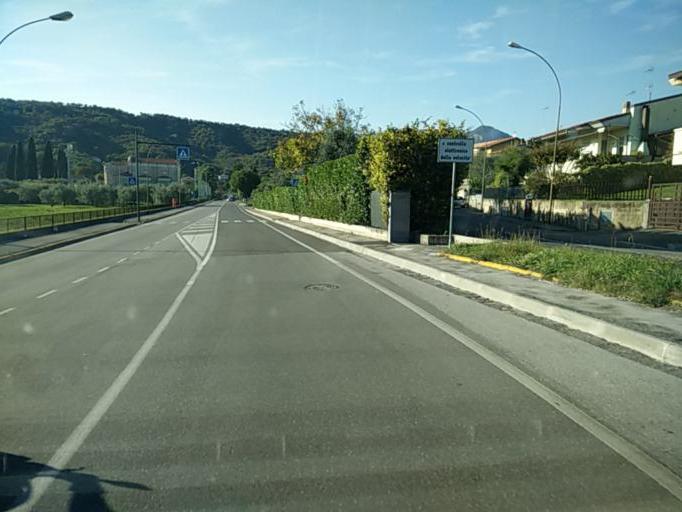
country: IT
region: Lombardy
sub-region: Provincia di Brescia
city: Cunettone-Villa
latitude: 45.5908
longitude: 10.5125
